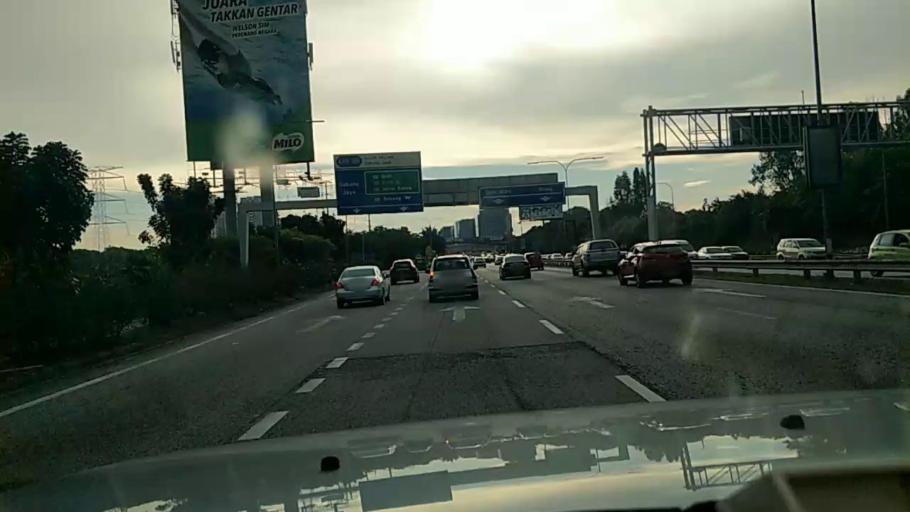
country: MY
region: Selangor
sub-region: Petaling
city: Petaling Jaya
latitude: 3.0836
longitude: 101.5986
